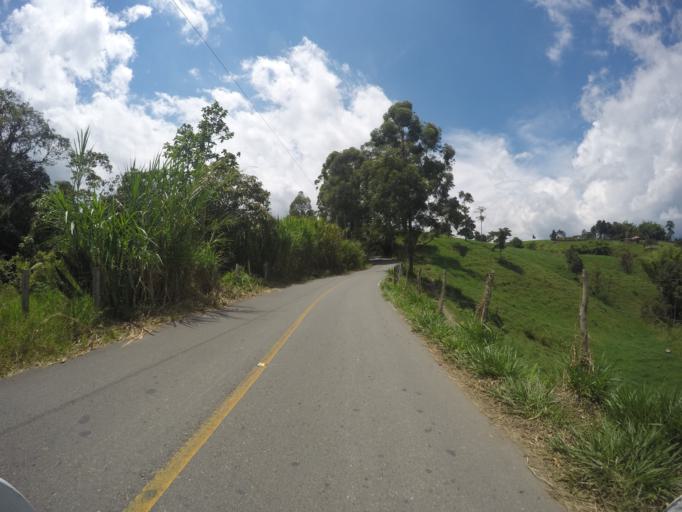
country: CO
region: Quindio
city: Filandia
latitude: 4.6327
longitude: -75.6928
